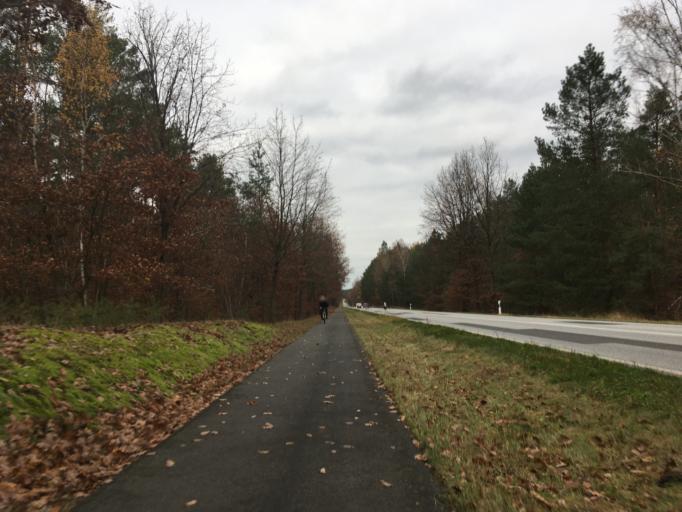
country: DE
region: Brandenburg
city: Mixdorf
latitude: 52.2034
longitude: 14.4562
